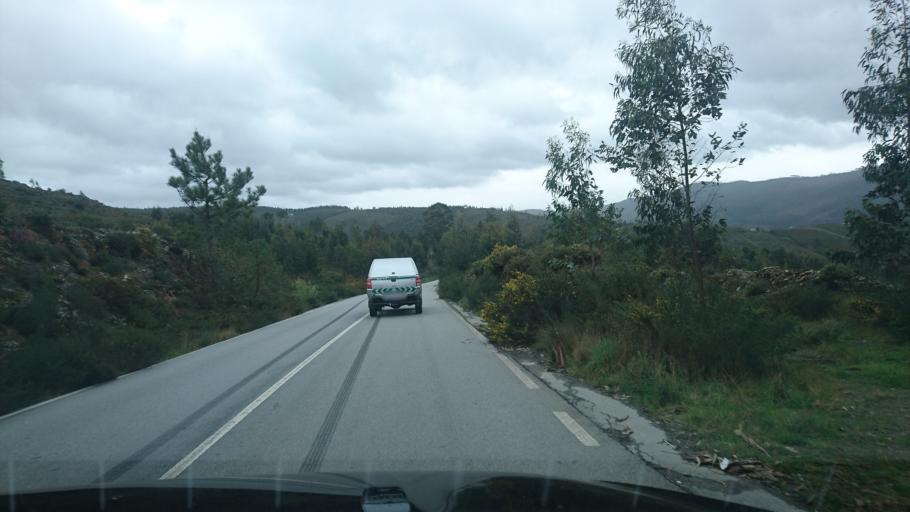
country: PT
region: Porto
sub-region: Paredes
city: Recarei
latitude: 41.1366
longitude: -8.4025
